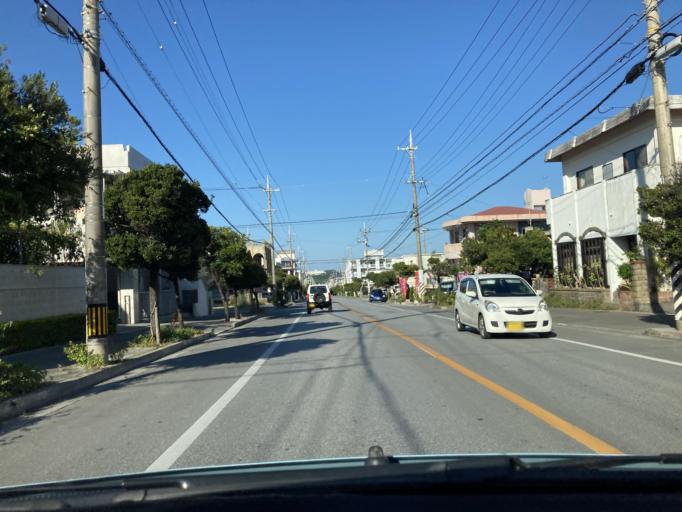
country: JP
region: Okinawa
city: Ginowan
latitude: 26.2789
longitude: 127.7803
